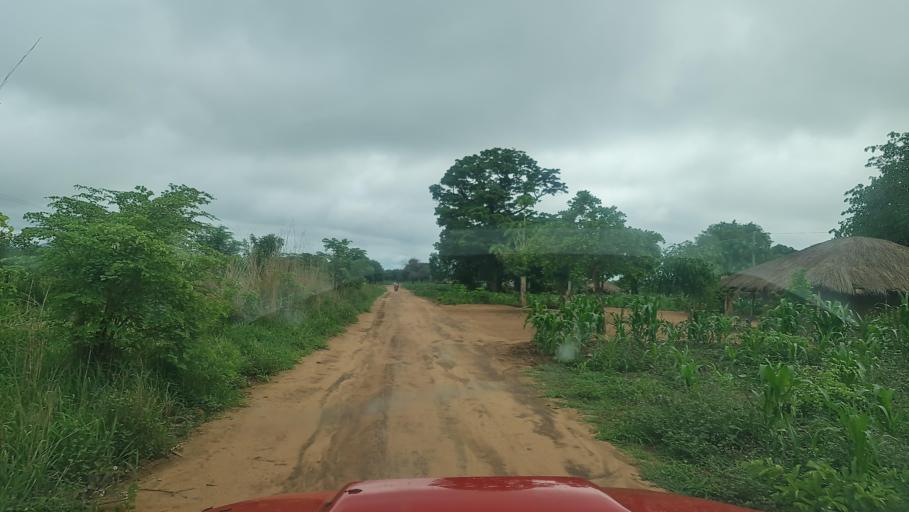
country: MW
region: Southern Region
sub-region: Nsanje District
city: Nsanje
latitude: -17.1958
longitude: 35.8451
